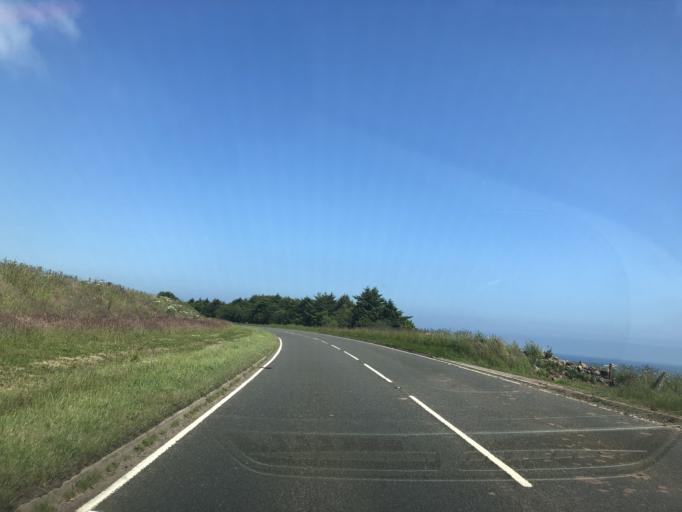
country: GB
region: Scotland
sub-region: Aberdeenshire
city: Stonehaven
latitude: 56.9223
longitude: -2.2064
